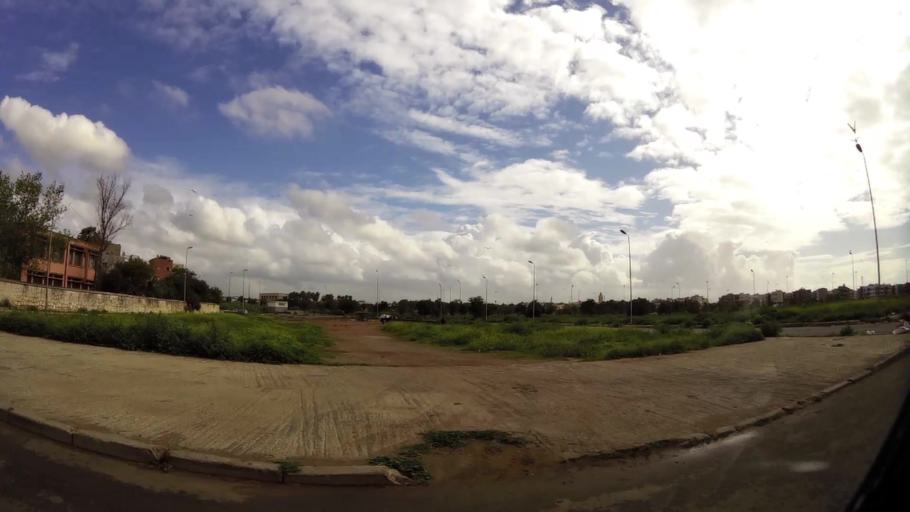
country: MA
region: Grand Casablanca
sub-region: Mohammedia
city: Mohammedia
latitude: 33.6807
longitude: -7.3793
